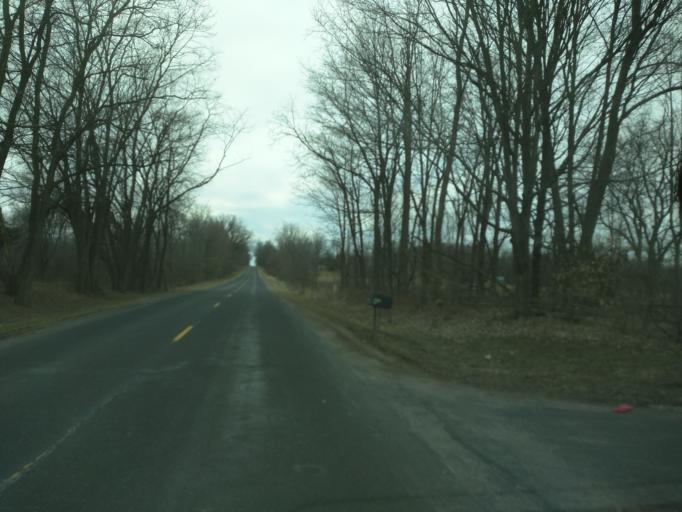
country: US
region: Michigan
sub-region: Ingham County
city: Okemos
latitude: 42.6693
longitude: -84.4157
